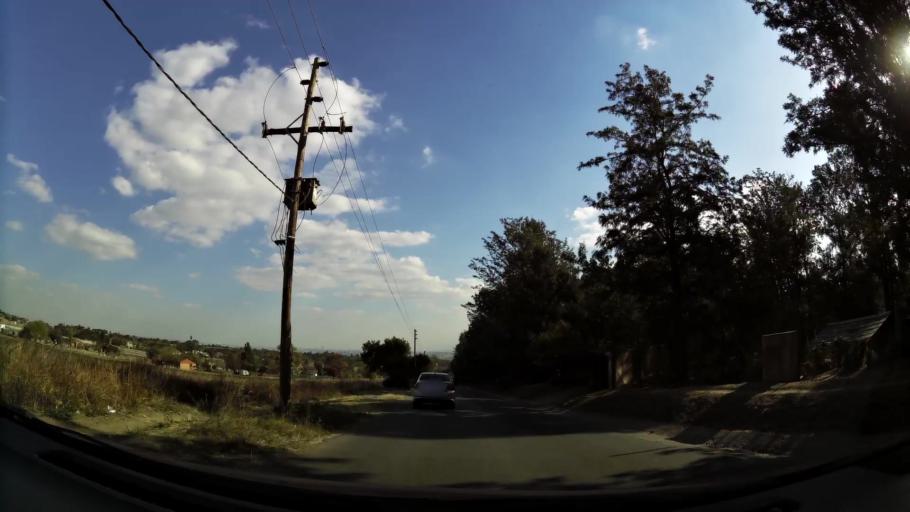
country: ZA
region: Gauteng
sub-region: City of Johannesburg Metropolitan Municipality
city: Midrand
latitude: -26.0165
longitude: 28.1551
